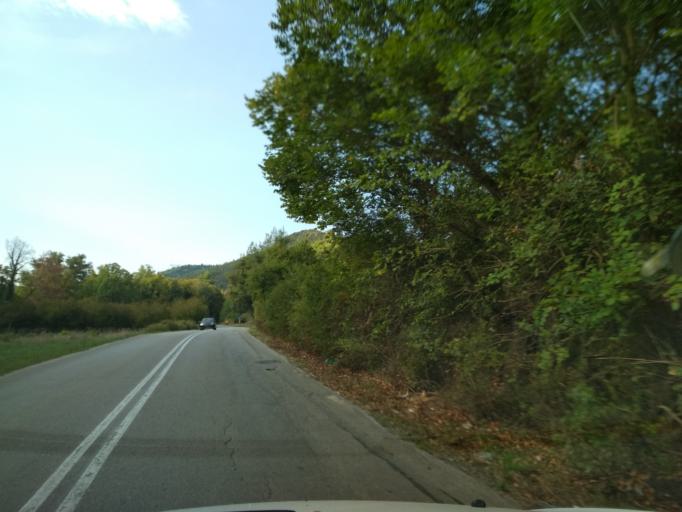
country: GR
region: Central Greece
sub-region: Nomos Evvoias
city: Mantoudi
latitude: 38.7809
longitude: 23.4702
